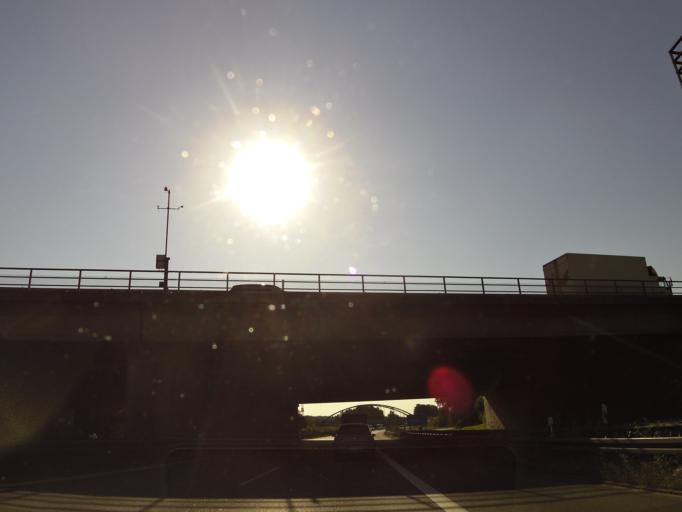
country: DE
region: Bavaria
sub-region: Regierungsbezirk Mittelfranken
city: Erlangen
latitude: 49.5598
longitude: 10.9912
